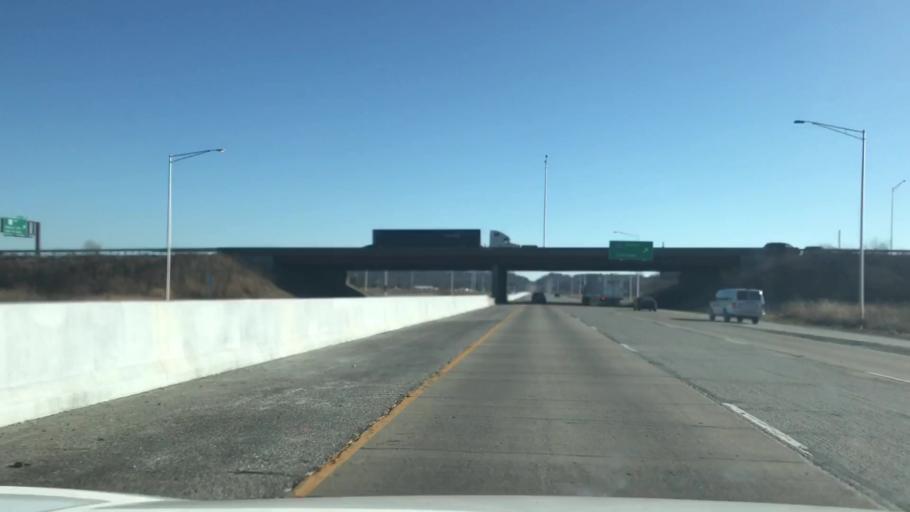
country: US
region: Illinois
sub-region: Saint Clair County
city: Alorton
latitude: 38.5833
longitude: -90.1089
